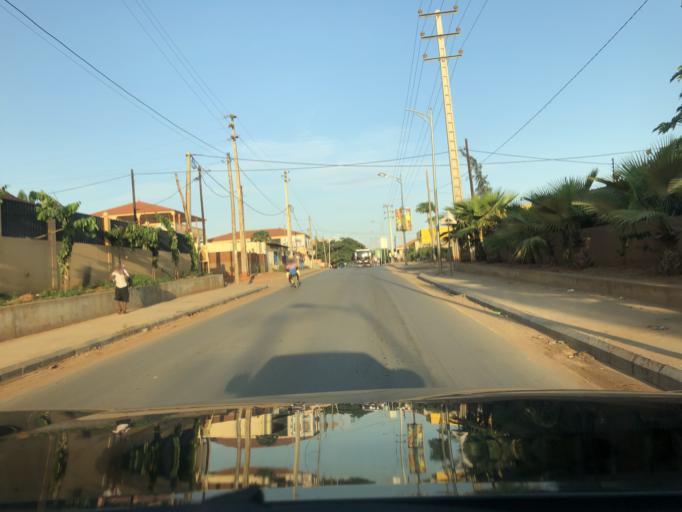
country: AO
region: Luanda
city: Luanda
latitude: -8.9514
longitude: 13.1742
